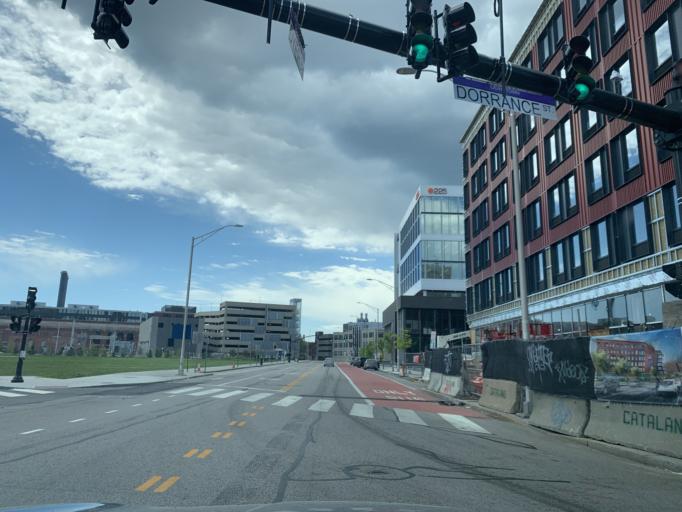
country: US
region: Rhode Island
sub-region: Providence County
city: Providence
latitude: 41.8213
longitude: -71.4082
